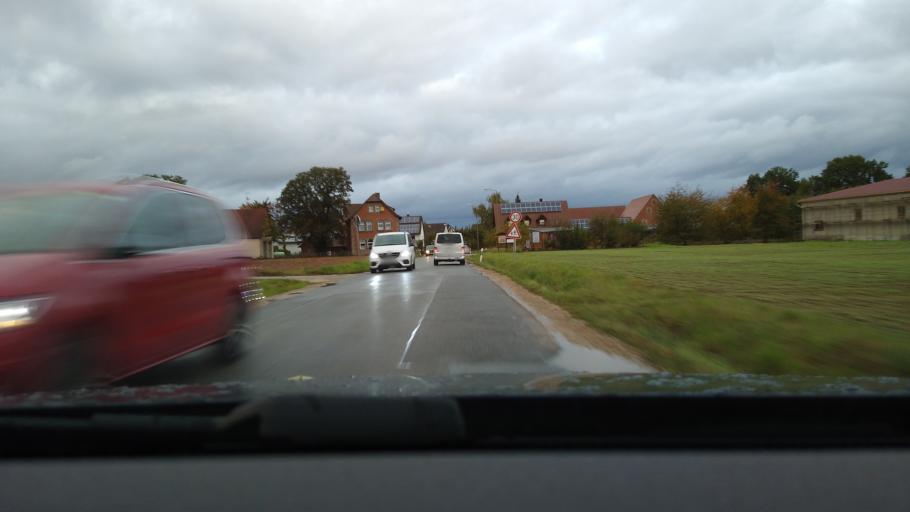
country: DE
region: Bavaria
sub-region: Regierungsbezirk Mittelfranken
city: Obermichelbach
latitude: 49.5373
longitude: 10.9597
